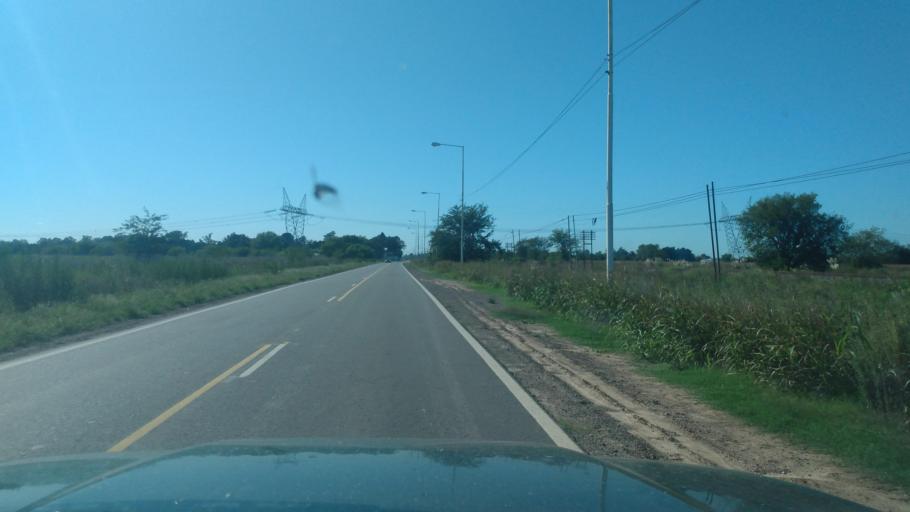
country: AR
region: Buenos Aires
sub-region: Partido de General Rodriguez
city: General Rodriguez
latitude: -34.5910
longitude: -59.0281
